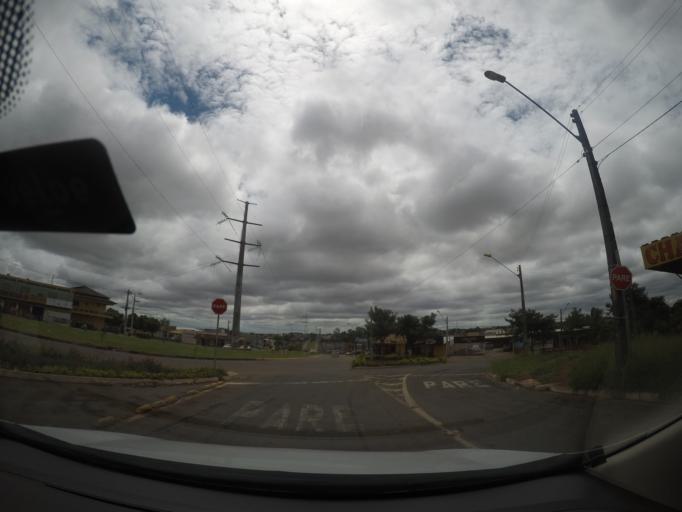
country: BR
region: Goias
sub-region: Goiania
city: Goiania
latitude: -16.7348
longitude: -49.3593
